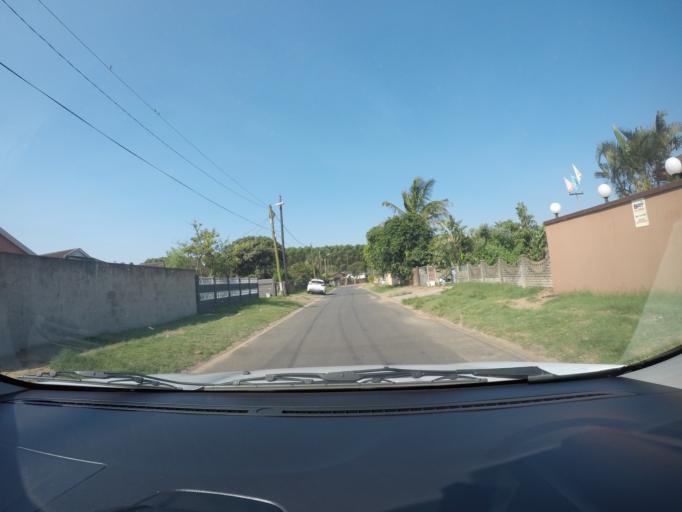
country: ZA
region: KwaZulu-Natal
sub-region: uThungulu District Municipality
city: Richards Bay
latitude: -28.7150
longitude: 32.0425
